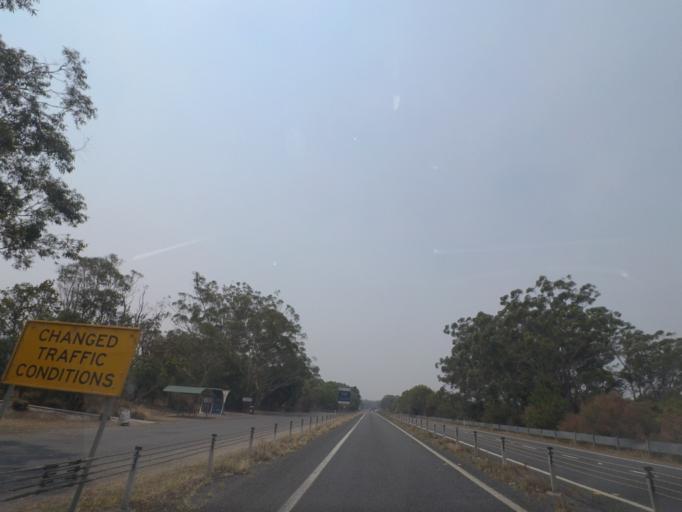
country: AU
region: New South Wales
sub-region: Ballina
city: Ballina
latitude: -28.9343
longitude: 153.4723
